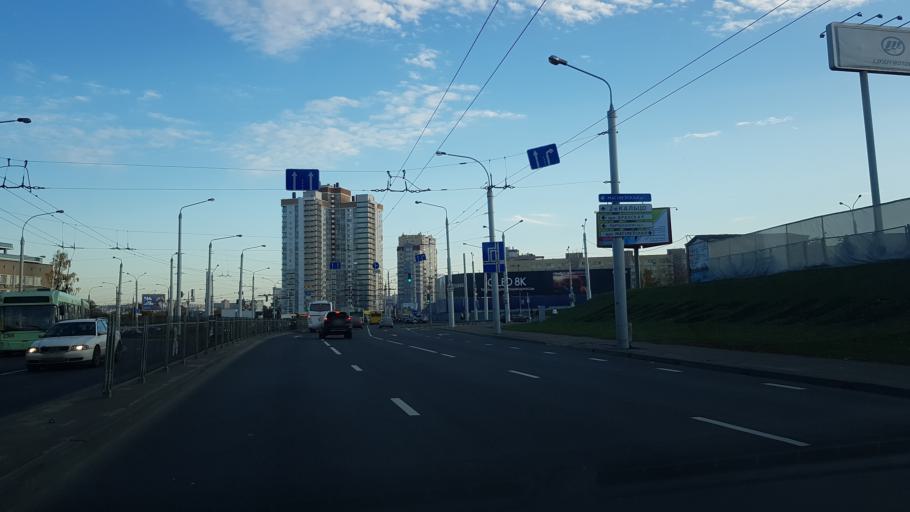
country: BY
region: Minsk
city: Minsk
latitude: 53.8866
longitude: 27.5659
